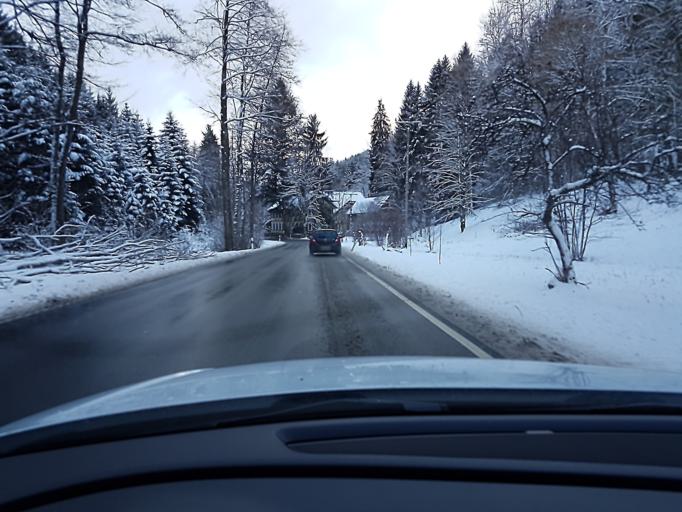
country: DE
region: Baden-Wuerttemberg
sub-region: Regierungsbezirk Stuttgart
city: Spiegelberg
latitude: 49.0533
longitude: 9.4383
